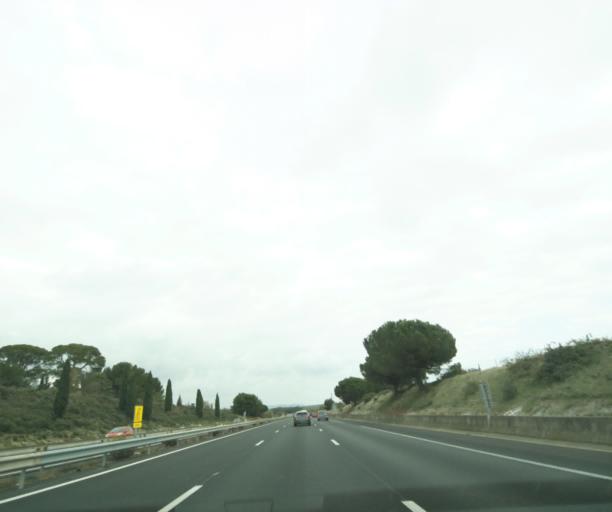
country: FR
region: Languedoc-Roussillon
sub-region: Departement de l'Herault
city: Pinet
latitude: 43.4222
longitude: 3.5407
